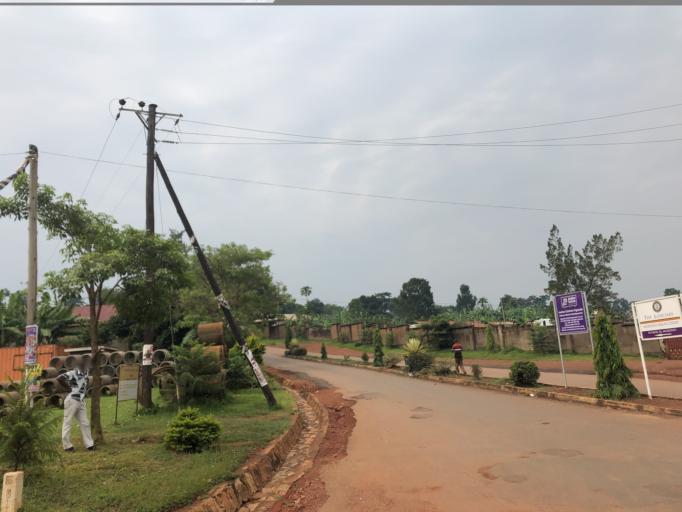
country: UG
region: Central Region
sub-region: Mukono District
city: Mukono
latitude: 0.3657
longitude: 32.7409
